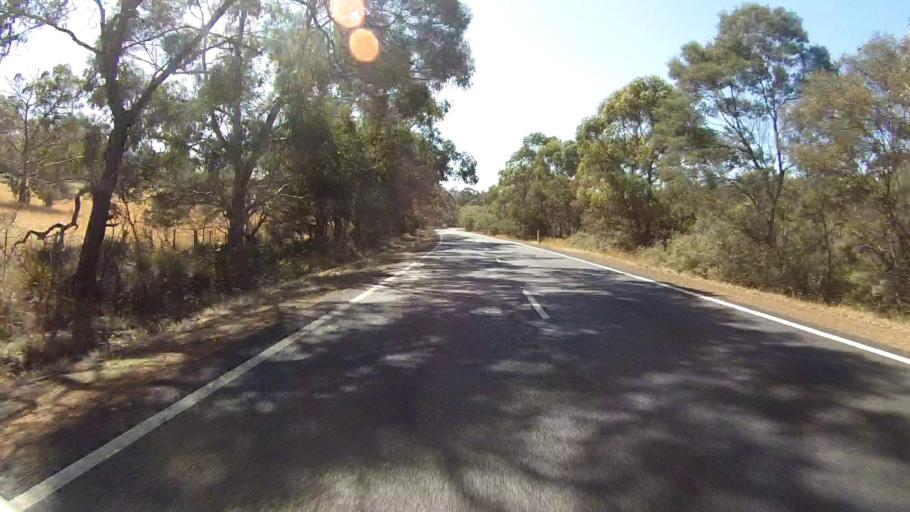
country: AU
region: Tasmania
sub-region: Sorell
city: Sorell
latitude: -42.4123
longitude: 147.9341
